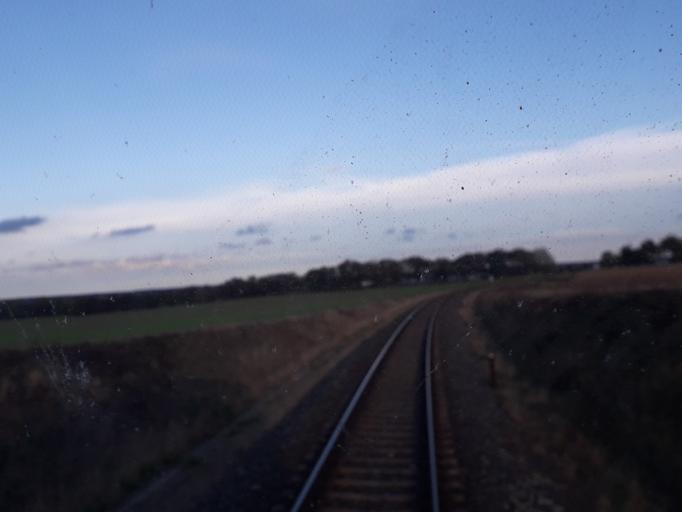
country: DE
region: Brandenburg
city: Wittstock
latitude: 53.1584
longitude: 12.4281
